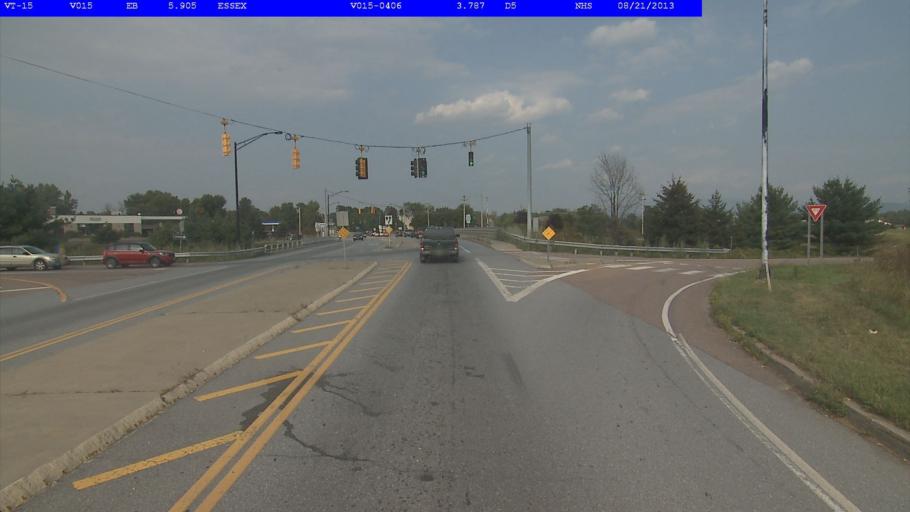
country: US
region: Vermont
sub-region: Chittenden County
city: Essex Junction
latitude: 44.5066
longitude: -73.0892
